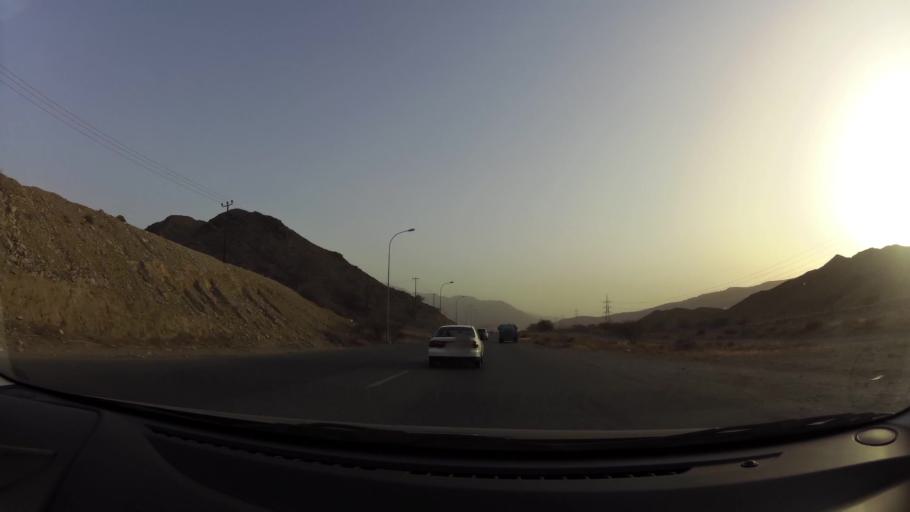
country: OM
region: Muhafazat Masqat
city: Bawshar
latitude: 23.4971
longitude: 58.3254
